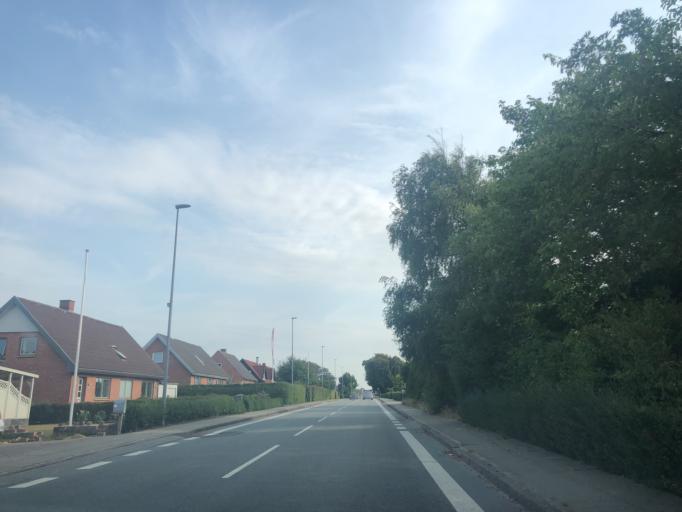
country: DK
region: Central Jutland
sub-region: Skive Kommune
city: Skive
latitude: 56.6201
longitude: 8.8801
